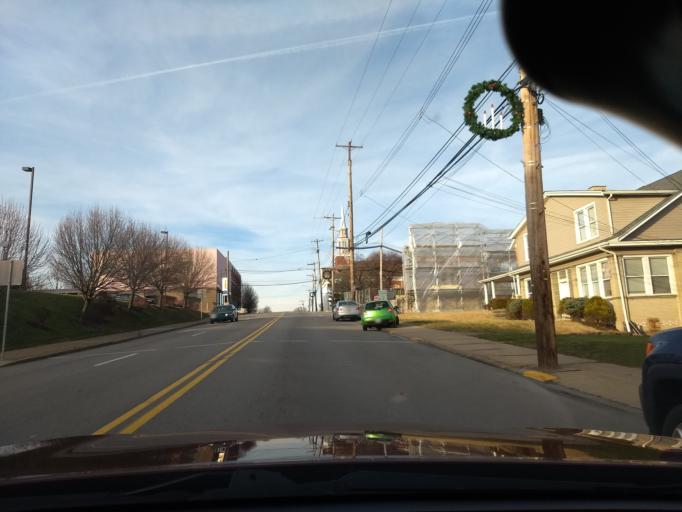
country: US
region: Pennsylvania
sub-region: Allegheny County
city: Brentwood
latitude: 40.3711
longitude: -79.9752
